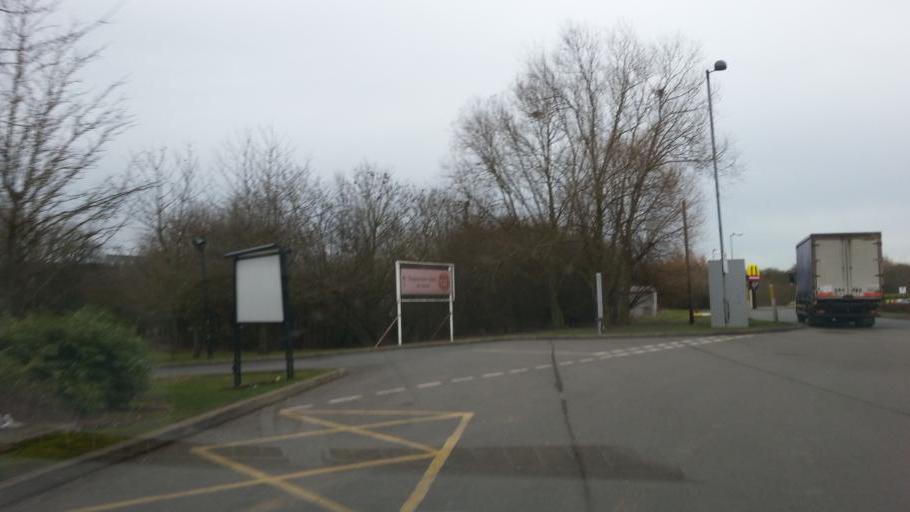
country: GB
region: England
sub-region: Cambridgeshire
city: Brampton
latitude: 52.3317
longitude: -0.2517
